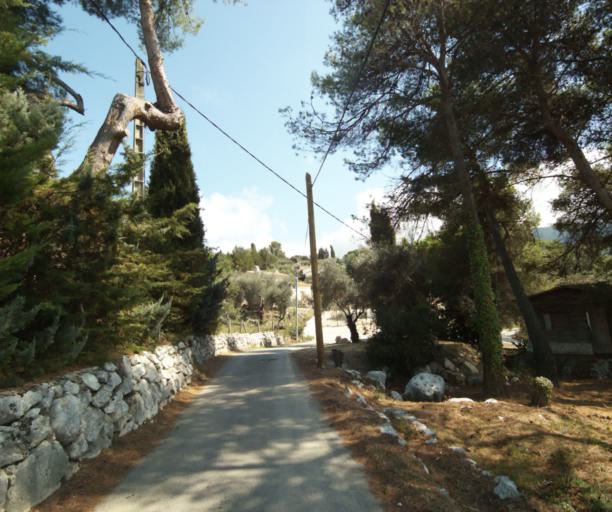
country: FR
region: Provence-Alpes-Cote d'Azur
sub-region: Departement des Alpes-Maritimes
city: Drap
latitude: 43.7549
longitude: 7.3446
